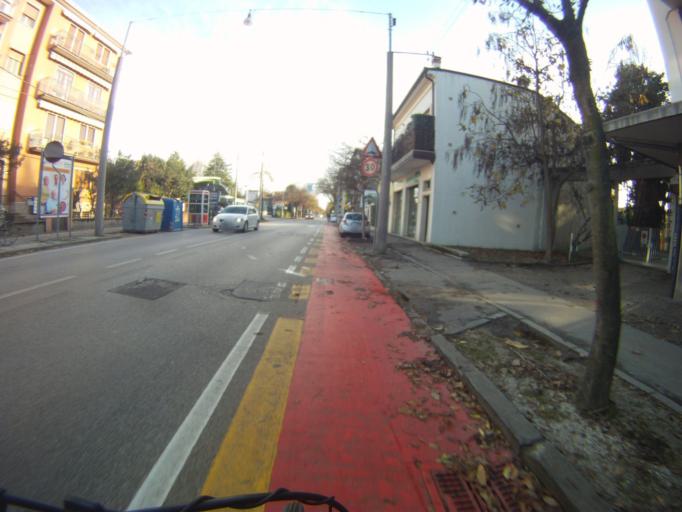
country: IT
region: Veneto
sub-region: Provincia di Padova
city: Padova
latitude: 45.3933
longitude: 11.8909
